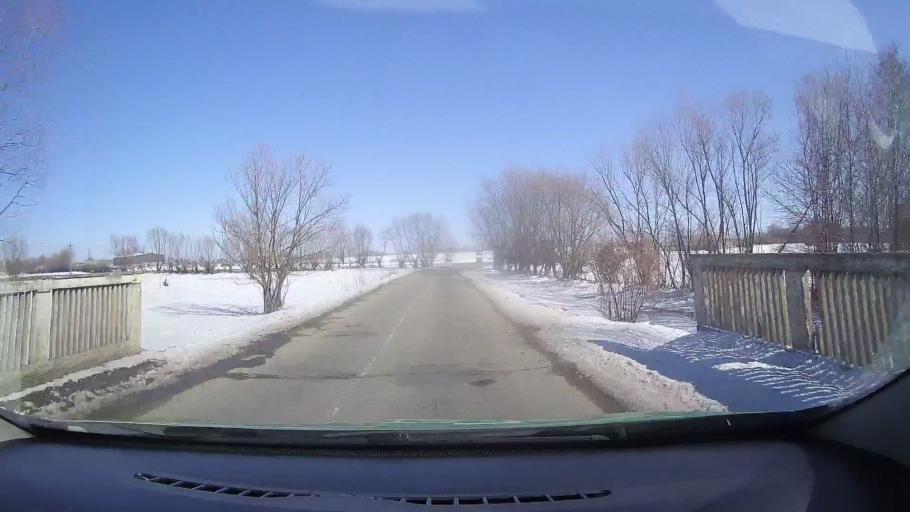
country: RO
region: Brasov
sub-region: Comuna Harseni
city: Harseni
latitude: 45.7341
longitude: 25.0014
